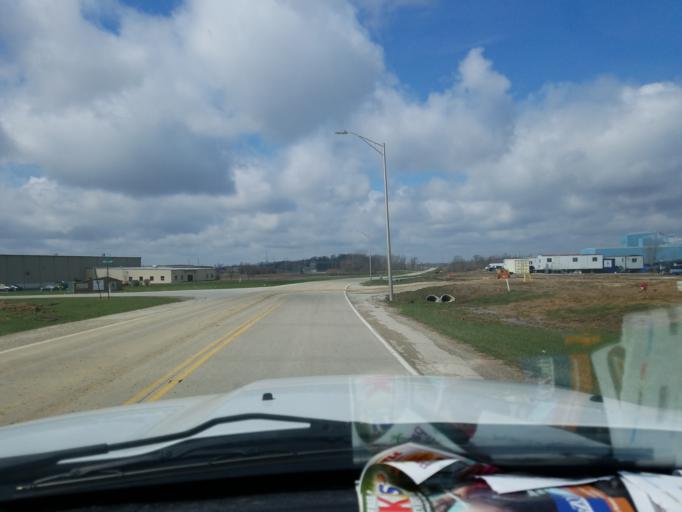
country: US
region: Indiana
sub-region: Sullivan County
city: Farmersburg
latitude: 39.3409
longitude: -87.4101
